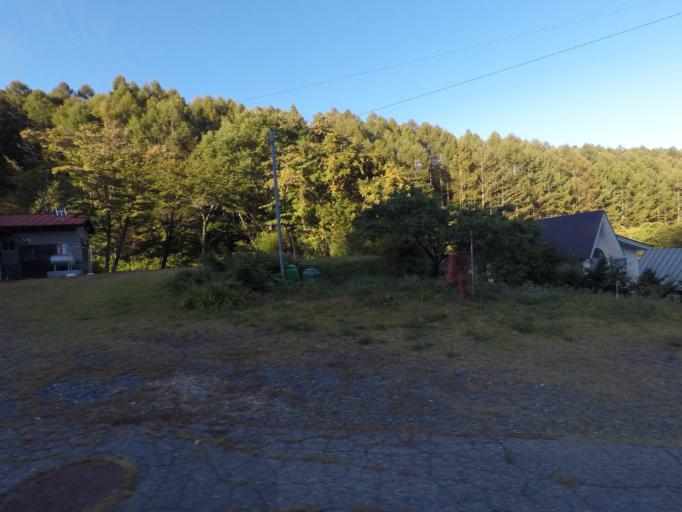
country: JP
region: Nagano
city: Ina
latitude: 35.9653
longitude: 137.7412
